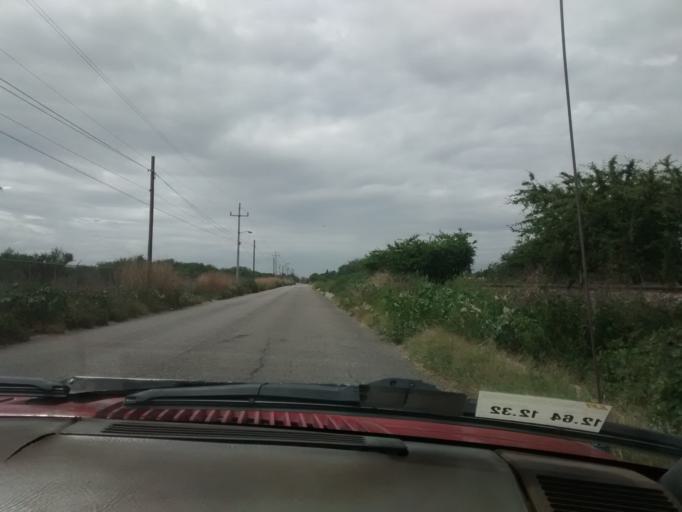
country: MX
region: Puebla
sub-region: Santiago Miahuatlan
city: San Jose Monte Chiquito
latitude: 18.4972
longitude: -97.4228
